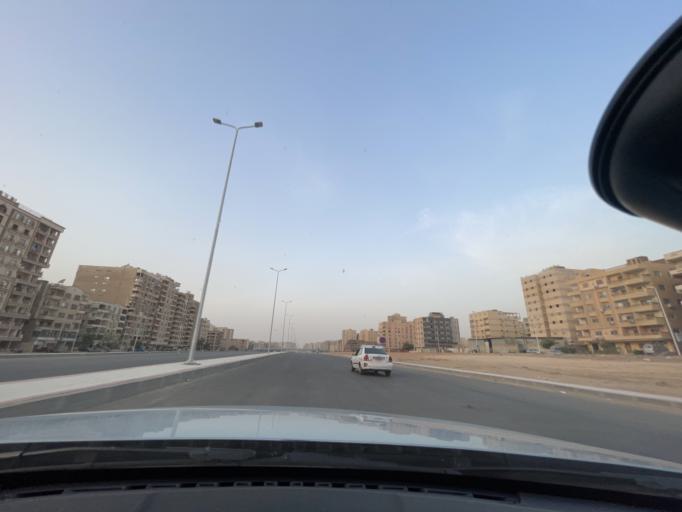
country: EG
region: Muhafazat al Qahirah
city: Cairo
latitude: 30.0528
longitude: 31.3708
